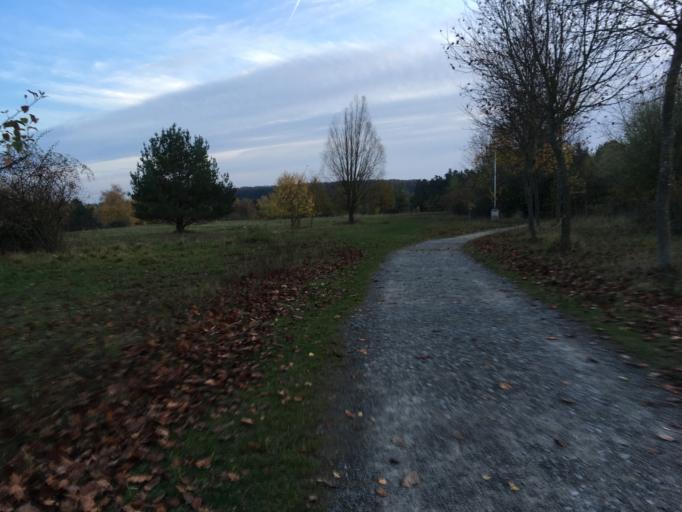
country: DE
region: Baden-Wuerttemberg
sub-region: Regierungsbezirk Stuttgart
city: Weinsberg
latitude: 49.1290
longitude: 9.2727
